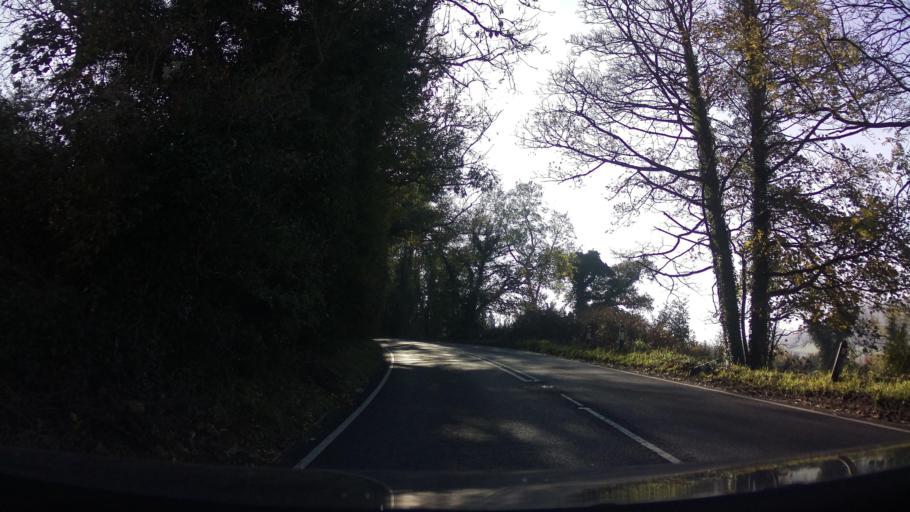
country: GB
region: England
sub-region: Bath and North East Somerset
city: Freshford
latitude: 51.3875
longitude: -2.3033
